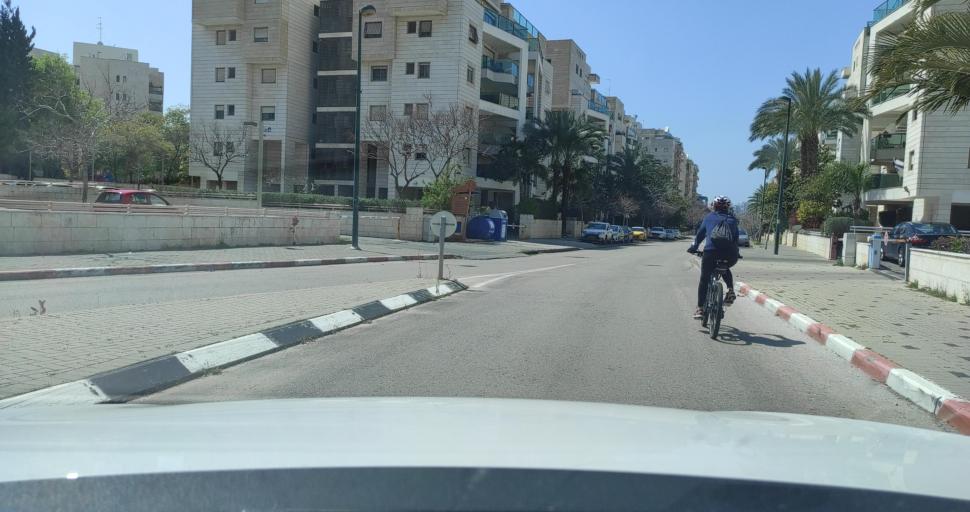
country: IL
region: Central District
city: Nordiyya
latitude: 32.2977
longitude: 34.8732
